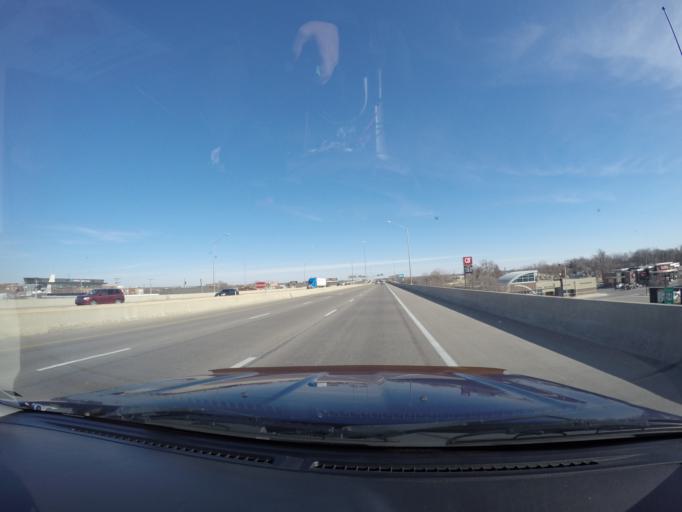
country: US
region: Kansas
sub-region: Sedgwick County
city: Wichita
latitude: 37.6788
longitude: -97.3356
